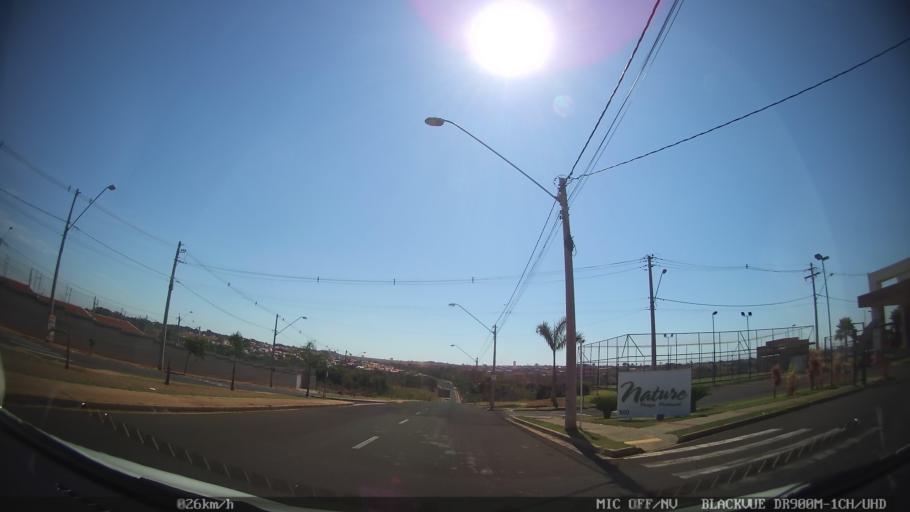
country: BR
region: Sao Paulo
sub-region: Sao Jose Do Rio Preto
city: Sao Jose do Rio Preto
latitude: -20.7630
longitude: -49.4200
